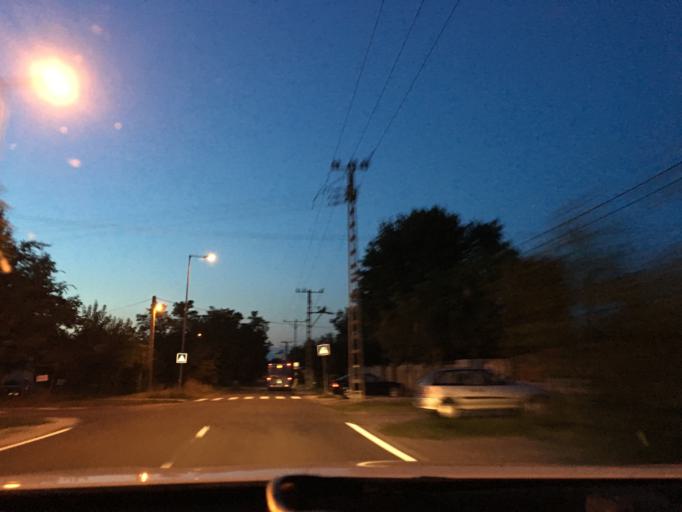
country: HU
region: Budapest
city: Budapest XVII. keruelet
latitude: 47.4597
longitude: 19.2460
